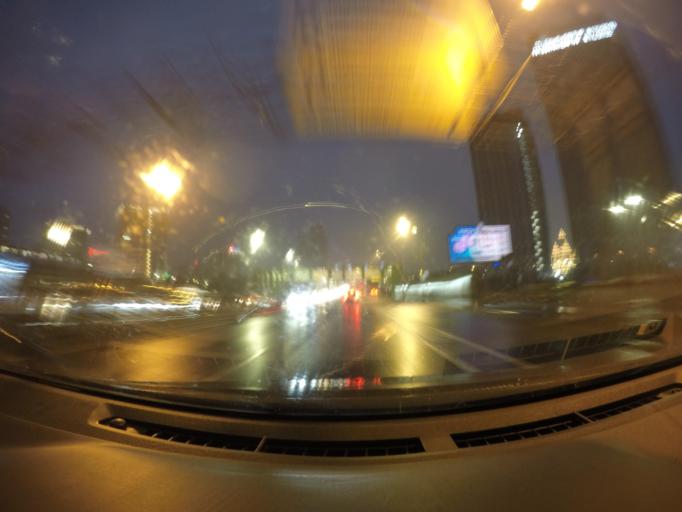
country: RU
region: Moskovskaya
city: Kozhukhovo
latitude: 55.6901
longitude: 37.6659
